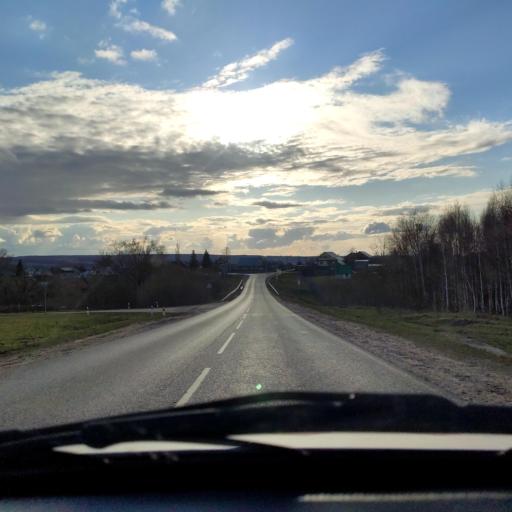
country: RU
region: Bashkortostan
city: Avdon
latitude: 54.5607
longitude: 55.6589
